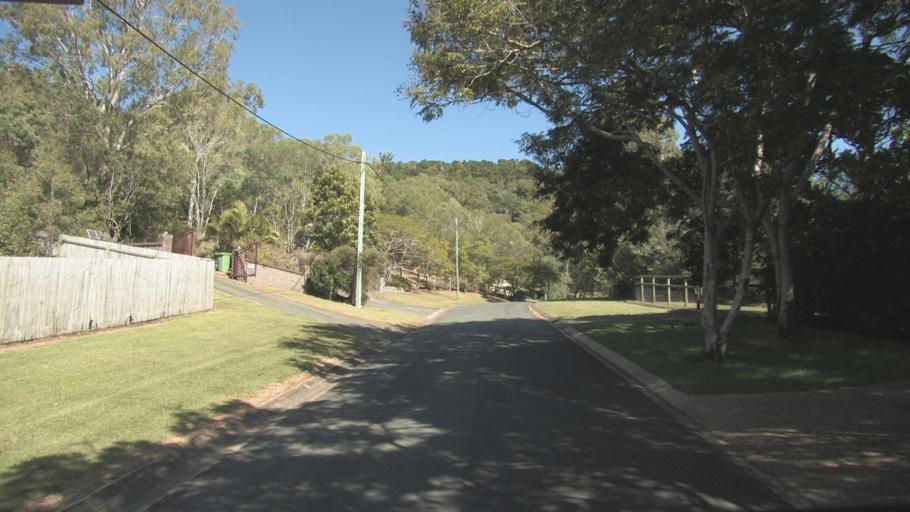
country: AU
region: Queensland
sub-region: Logan
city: Windaroo
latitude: -27.7431
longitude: 153.1814
